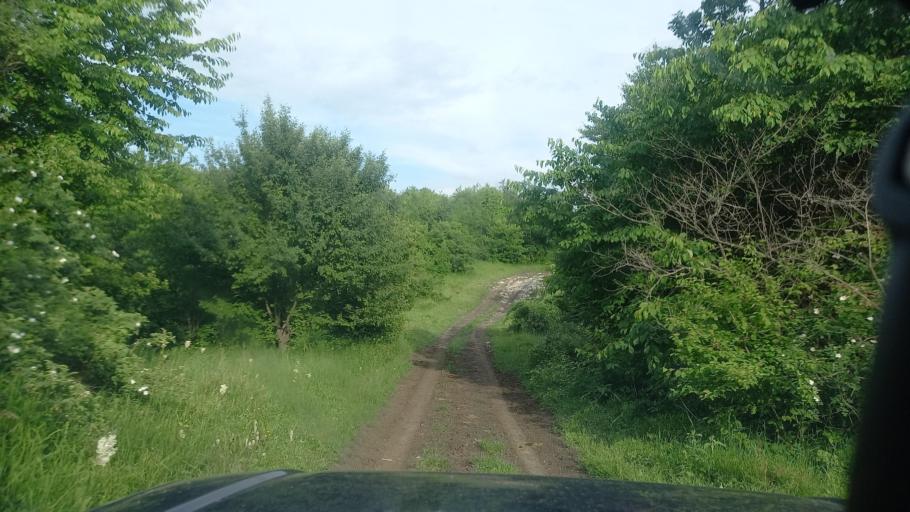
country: RU
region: Karachayevo-Cherkesiya
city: Kurdzhinovo
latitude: 44.1259
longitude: 41.0794
